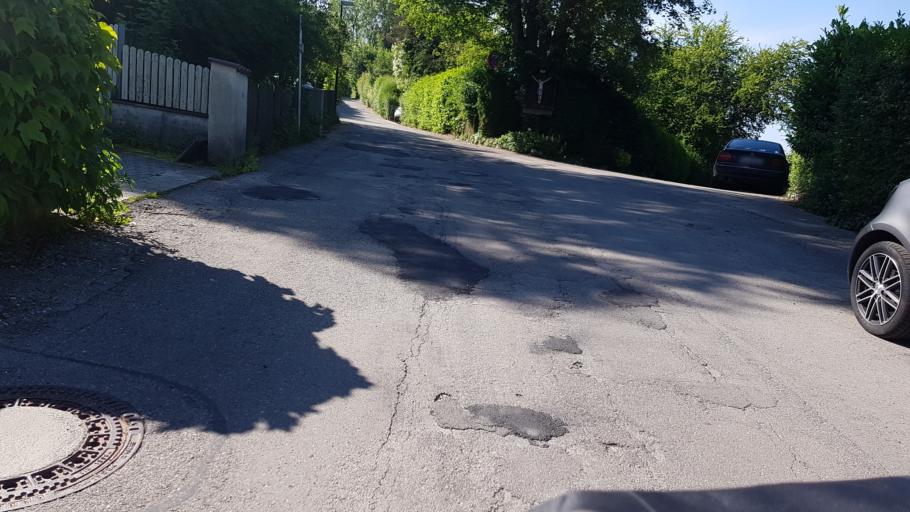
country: DE
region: Bavaria
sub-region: Upper Bavaria
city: Starnberg
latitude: 48.0254
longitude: 11.3717
